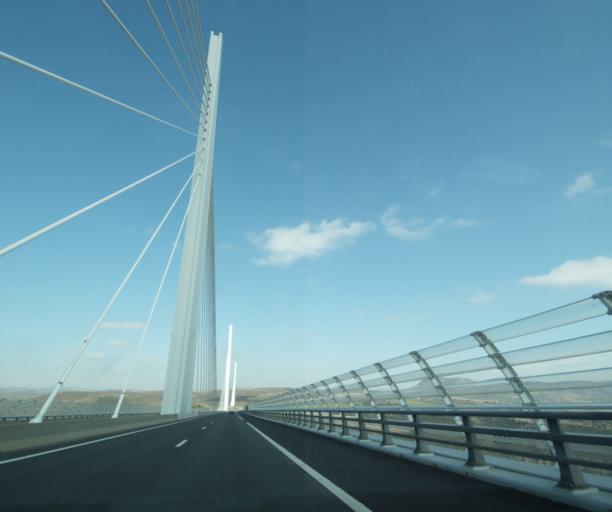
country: FR
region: Midi-Pyrenees
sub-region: Departement de l'Aveyron
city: Creissels
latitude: 44.0831
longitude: 3.0223
